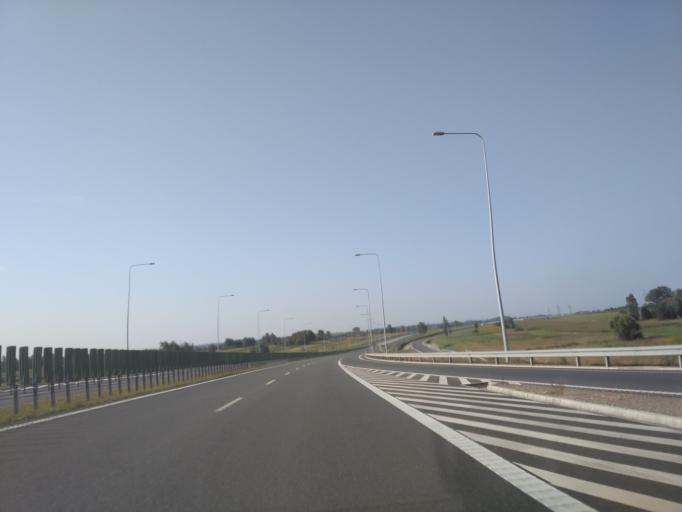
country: PL
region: Subcarpathian Voivodeship
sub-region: Powiat rzeszowski
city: Sokolow Malopolski
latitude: 50.2276
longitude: 22.1393
